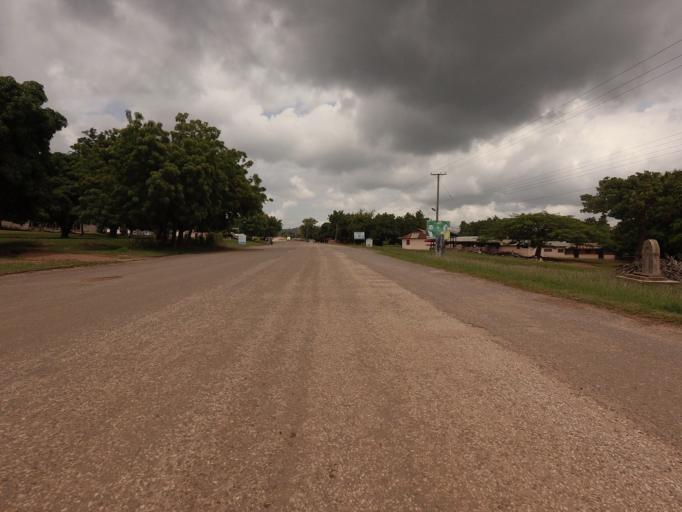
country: GH
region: Volta
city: Ho
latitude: 6.6422
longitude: 0.2982
